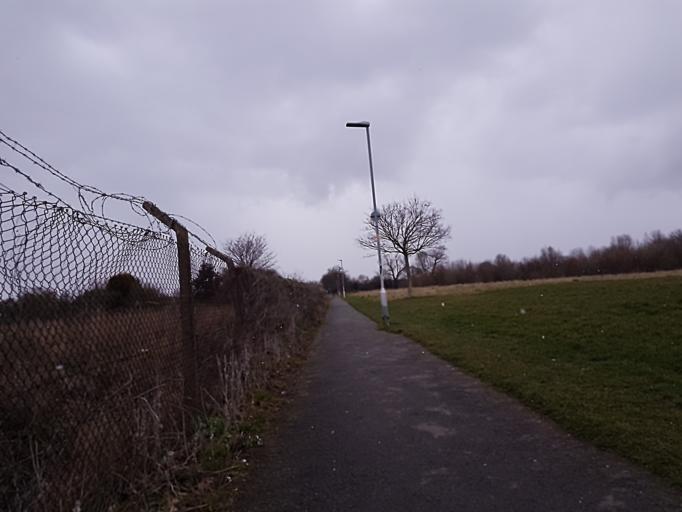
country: GB
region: England
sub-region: North East Lincolnshire
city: Grimbsy
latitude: 53.5571
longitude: -0.1033
